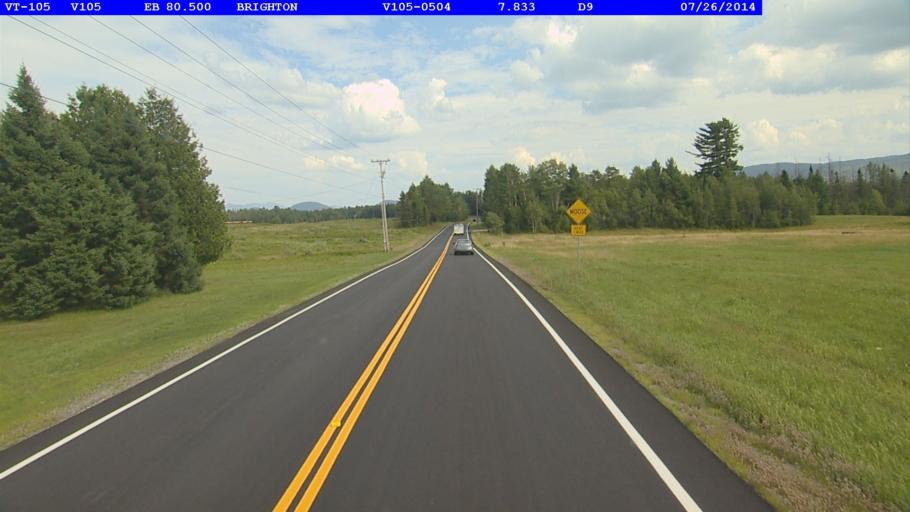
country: US
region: New Hampshire
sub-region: Coos County
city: Stratford
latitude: 44.7897
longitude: -71.8296
